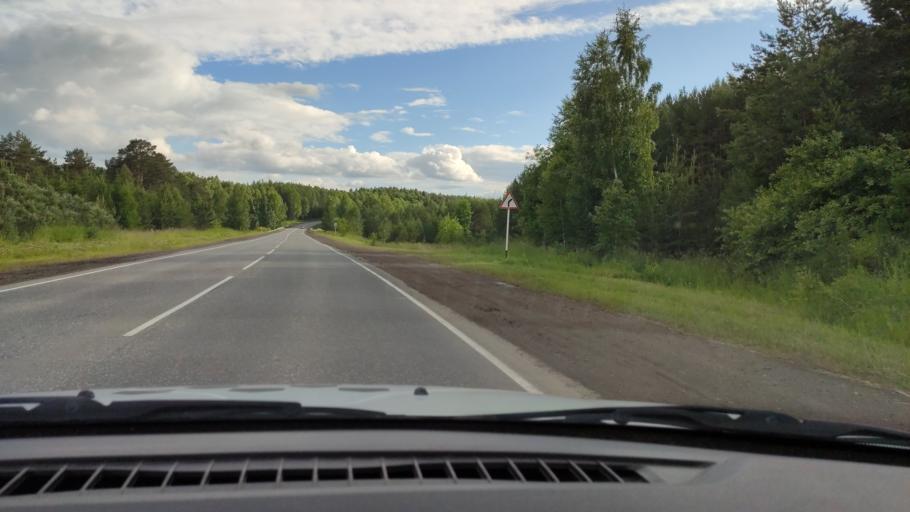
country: RU
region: Perm
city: Kungur
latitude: 57.4167
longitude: 56.9156
